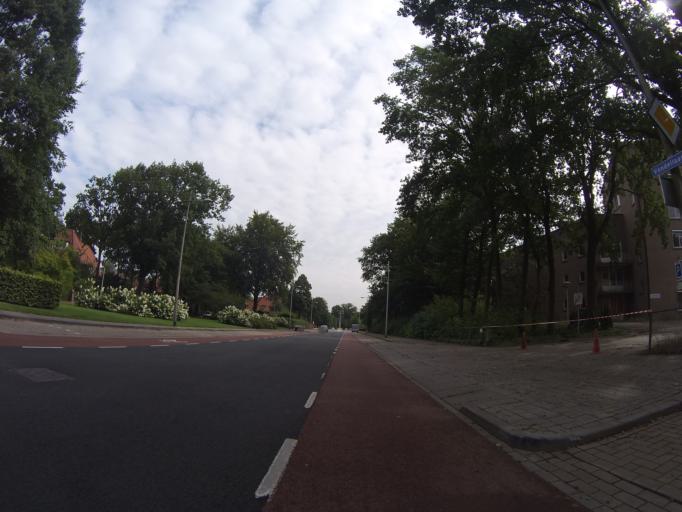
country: NL
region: Utrecht
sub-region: Gemeente Amersfoort
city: Amersfoort
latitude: 52.1452
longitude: 5.3703
